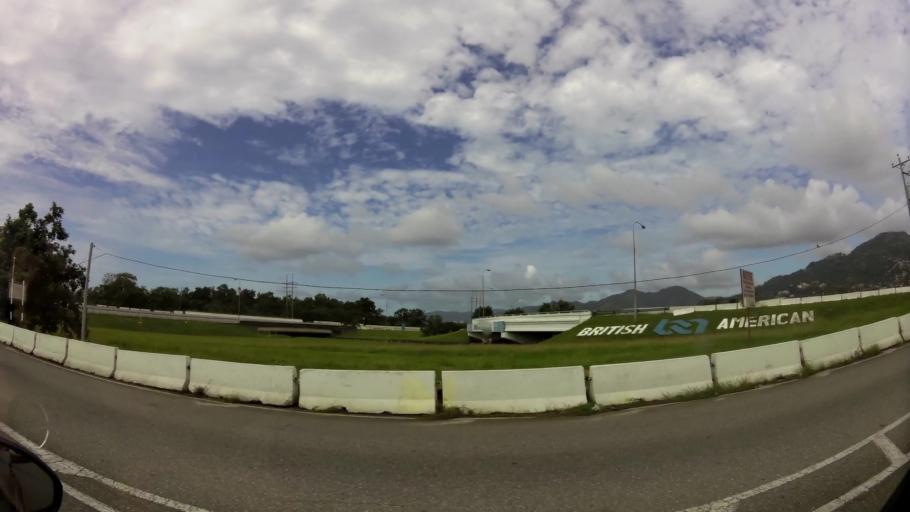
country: TT
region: City of Port of Spain
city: Mucurapo
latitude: 10.6616
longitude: -61.5345
